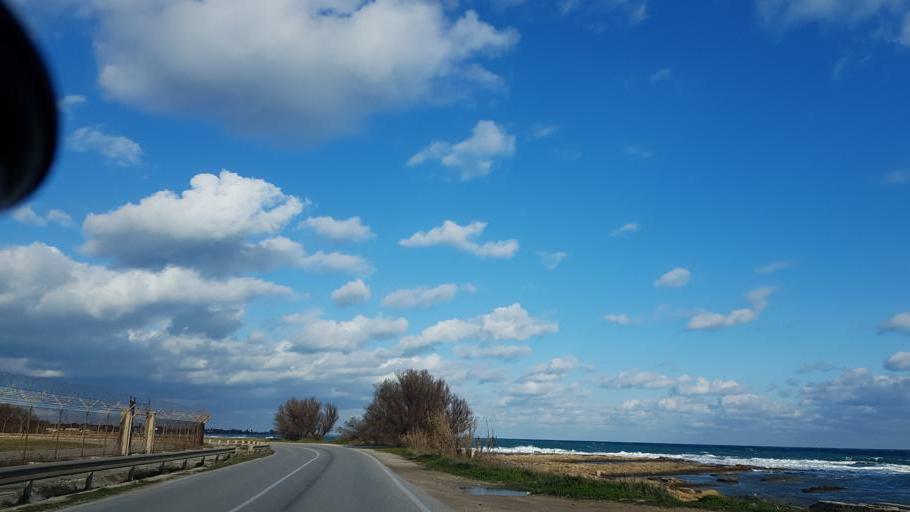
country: IT
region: Apulia
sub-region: Provincia di Brindisi
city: Materdomini
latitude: 40.6630
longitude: 17.9572
